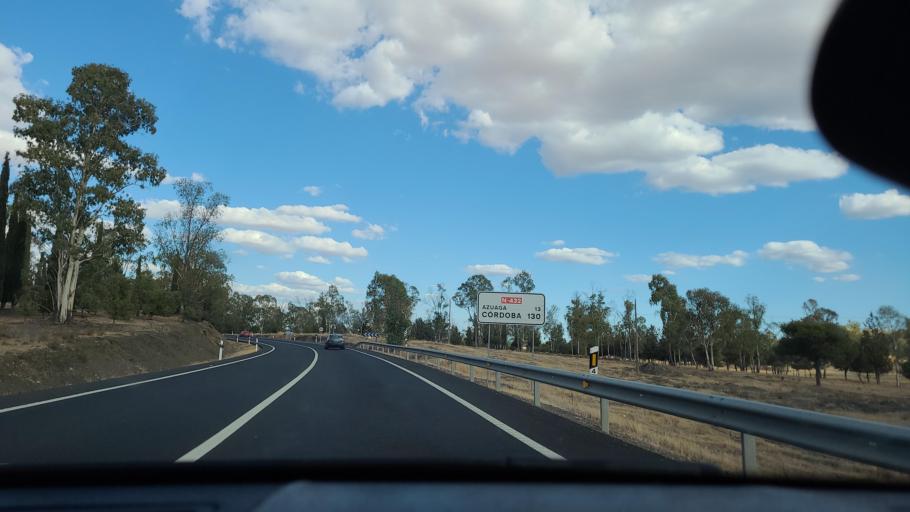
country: ES
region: Extremadura
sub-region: Provincia de Badajoz
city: Berlanga
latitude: 38.2727
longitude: -5.8131
